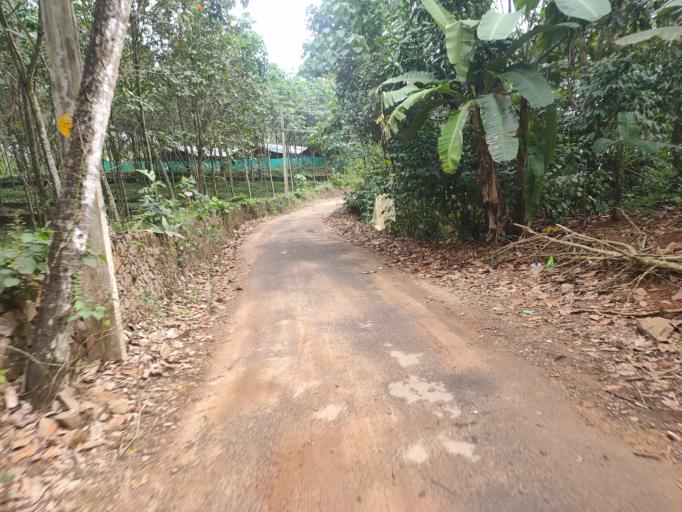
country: IN
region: Kerala
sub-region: Ernakulam
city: Kotamangalam
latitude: 10.0067
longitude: 76.6453
